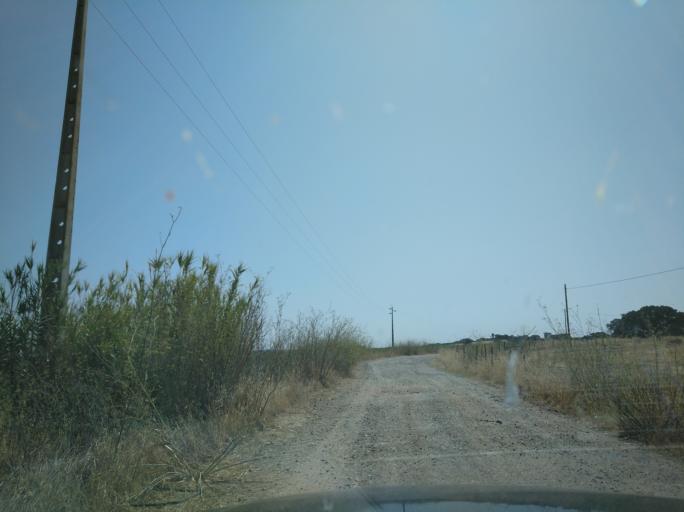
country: PT
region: Portalegre
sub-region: Campo Maior
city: Campo Maior
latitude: 39.0346
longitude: -6.9844
